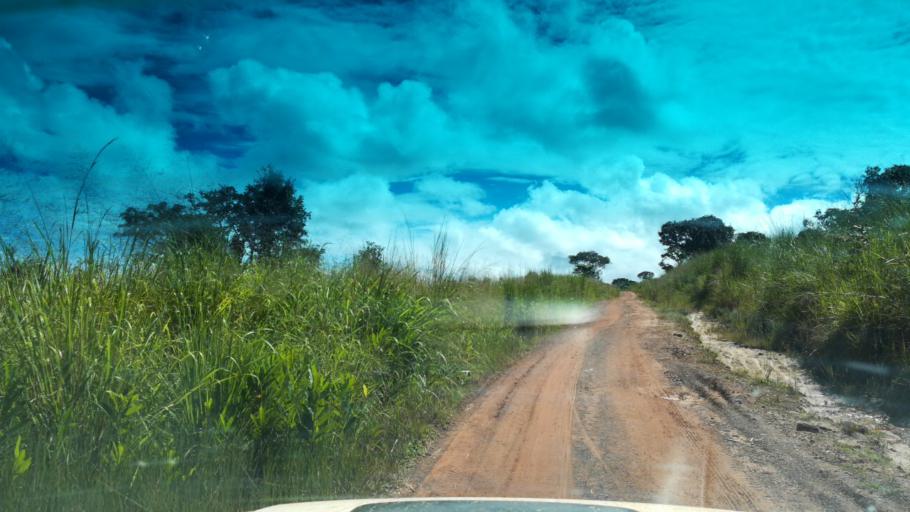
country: ZM
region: Northern
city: Kaputa
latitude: -7.7947
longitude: 29.2120
